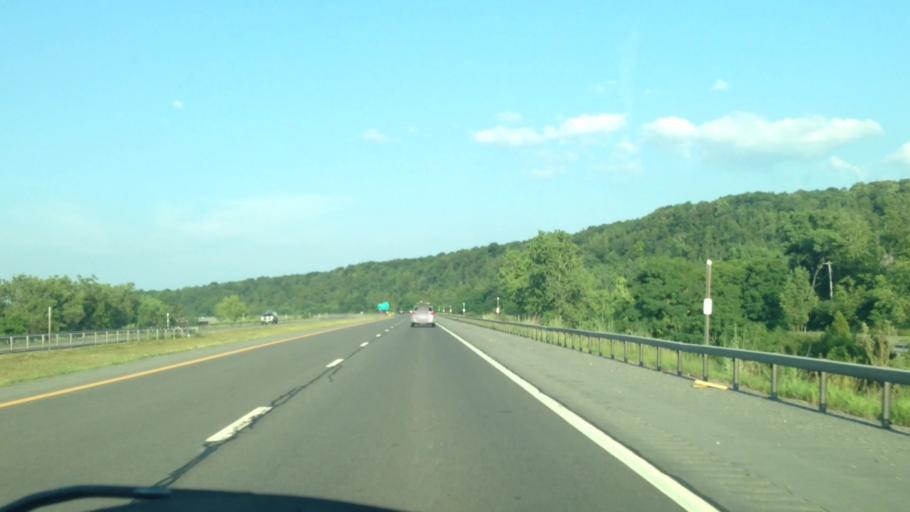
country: US
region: New York
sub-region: Onondaga County
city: Nedrow
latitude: 43.0038
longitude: -76.1031
